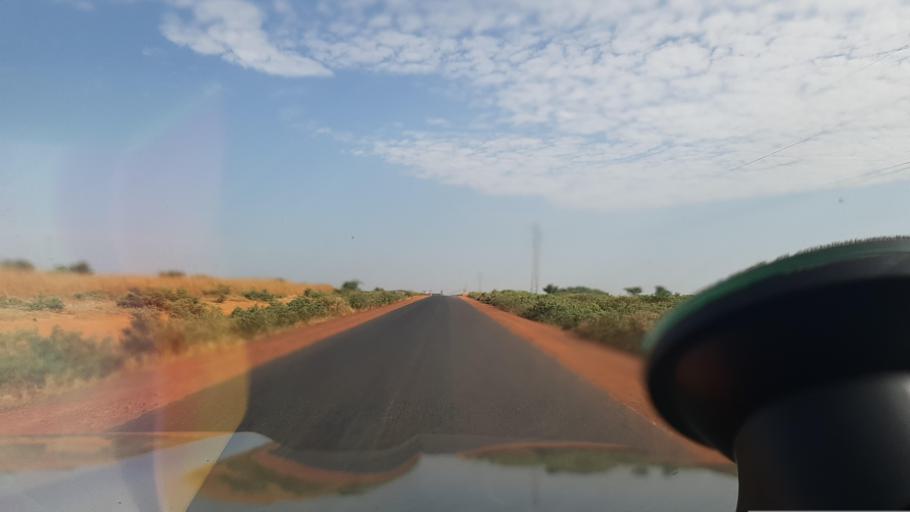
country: ML
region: Segou
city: Segou
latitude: 13.5434
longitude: -6.1205
